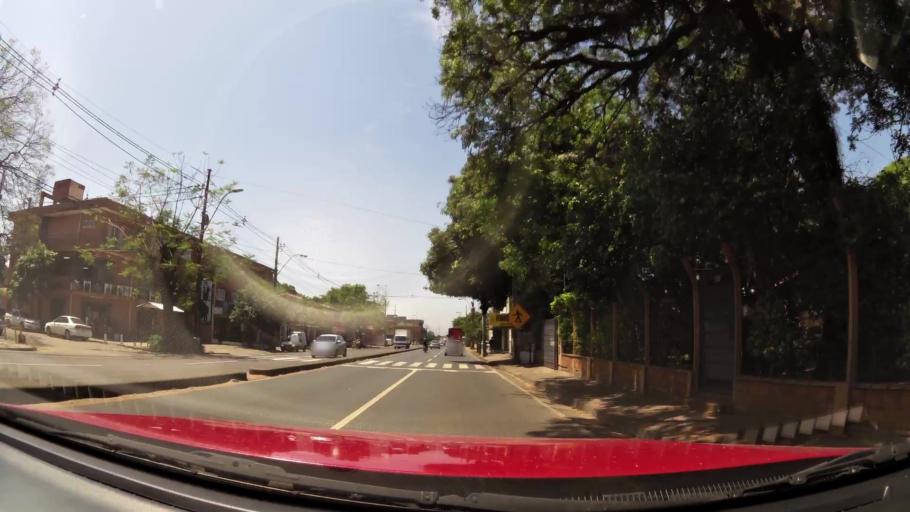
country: PY
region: Central
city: Fernando de la Mora
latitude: -25.3226
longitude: -57.5635
